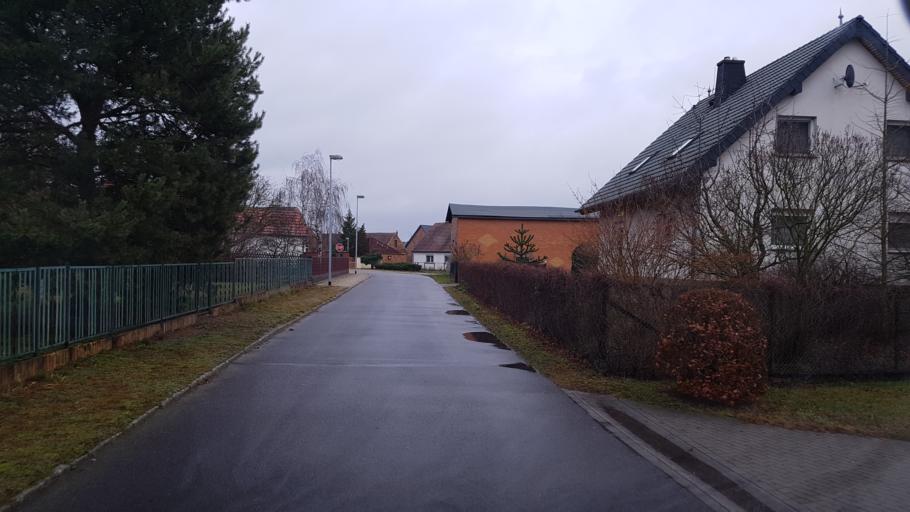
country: DE
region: Brandenburg
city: Altdobern
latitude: 51.6915
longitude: 14.0055
